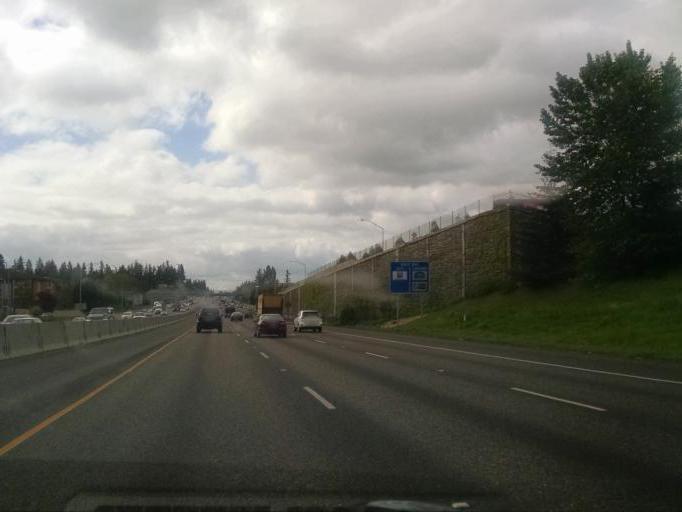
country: US
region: Oregon
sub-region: Washington County
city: Durham
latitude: 45.4200
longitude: -122.7442
